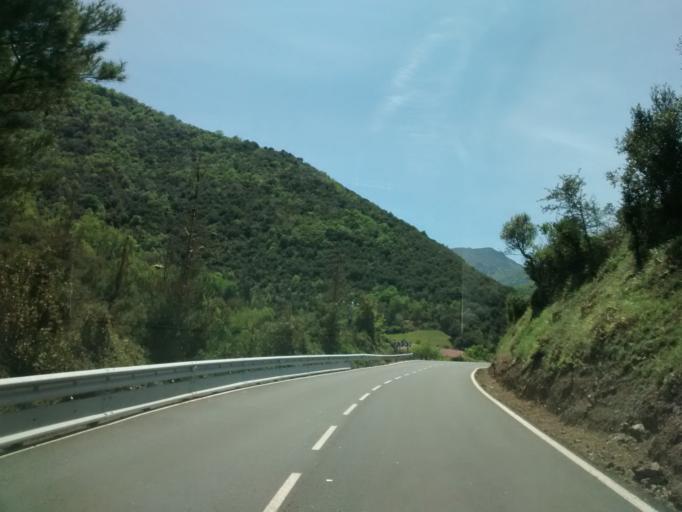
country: ES
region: Cantabria
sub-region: Provincia de Cantabria
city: Potes
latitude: 43.1056
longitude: -4.6409
